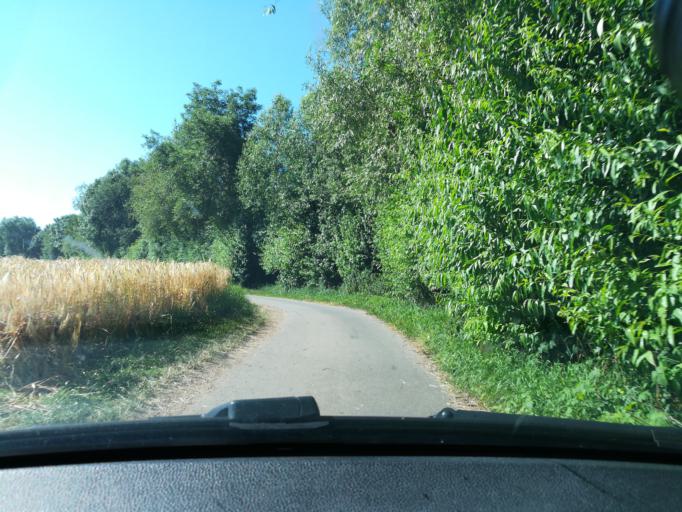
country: DE
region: North Rhine-Westphalia
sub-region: Regierungsbezirk Detmold
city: Minden
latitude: 52.3123
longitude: 8.9225
